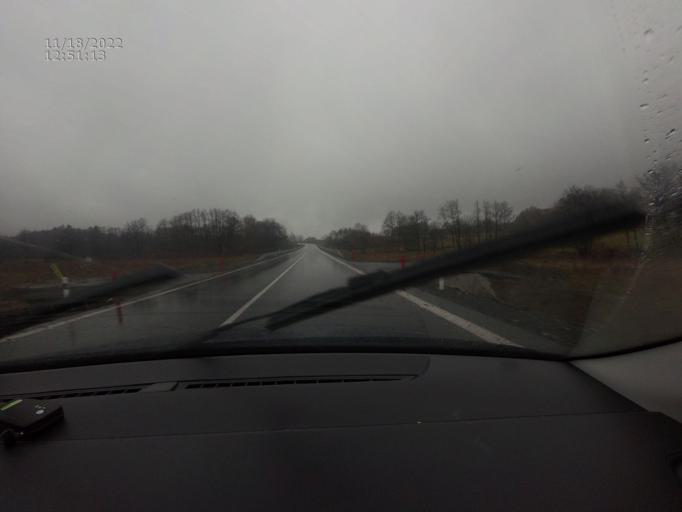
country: CZ
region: Plzensky
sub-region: Okres Klatovy
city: Kolinec
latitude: 49.3297
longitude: 13.4372
